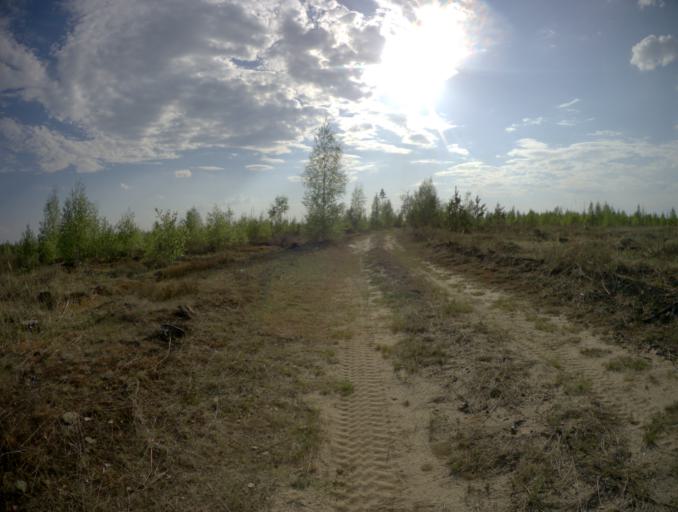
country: RU
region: Ivanovo
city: Talitsy
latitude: 56.4113
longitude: 42.2450
